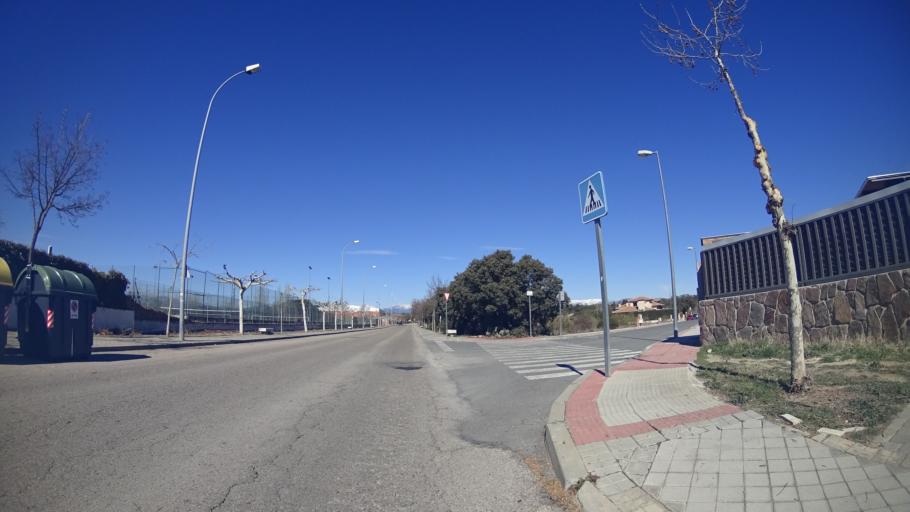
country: ES
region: Madrid
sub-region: Provincia de Madrid
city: Colmenarejo
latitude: 40.5495
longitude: -4.0113
